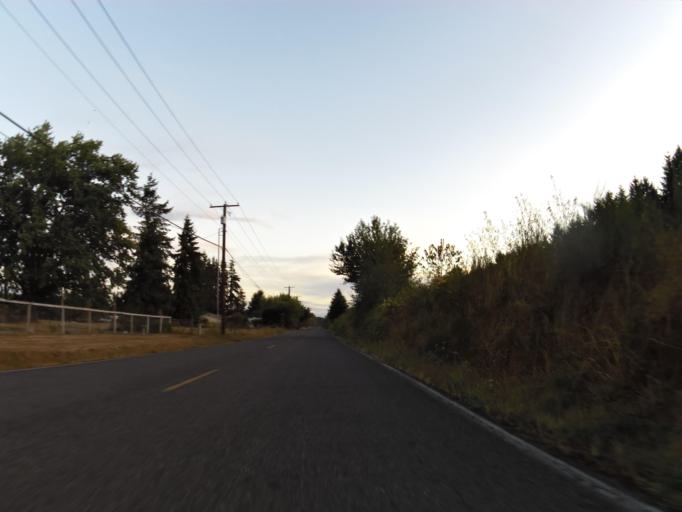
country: US
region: Washington
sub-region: Thurston County
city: Tenino
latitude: 46.8309
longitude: -122.8614
